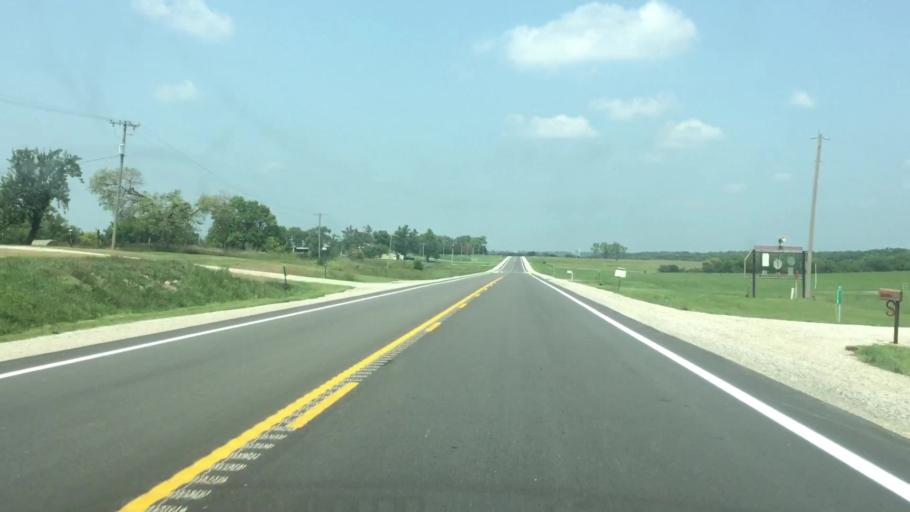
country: US
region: Kansas
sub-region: Anderson County
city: Garnett
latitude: 38.2986
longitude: -95.2489
